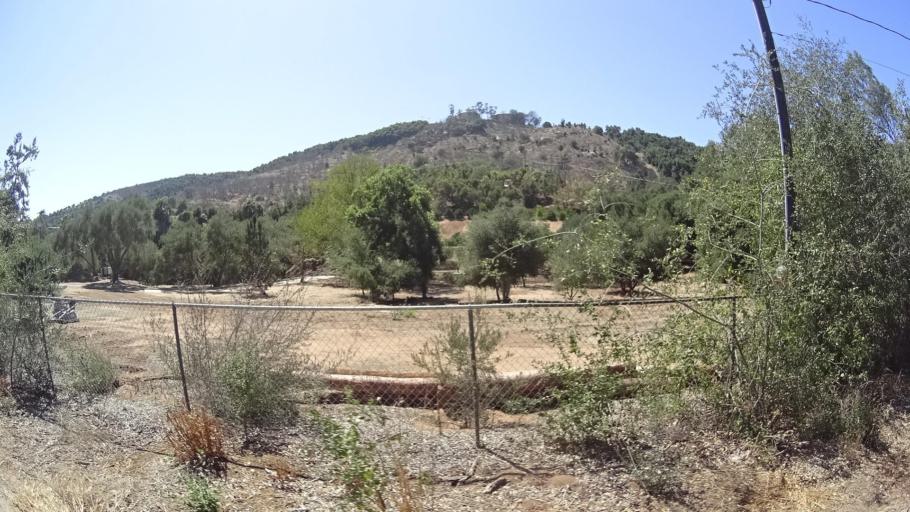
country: US
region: California
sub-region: San Diego County
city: Hidden Meadows
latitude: 33.3092
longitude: -117.0836
